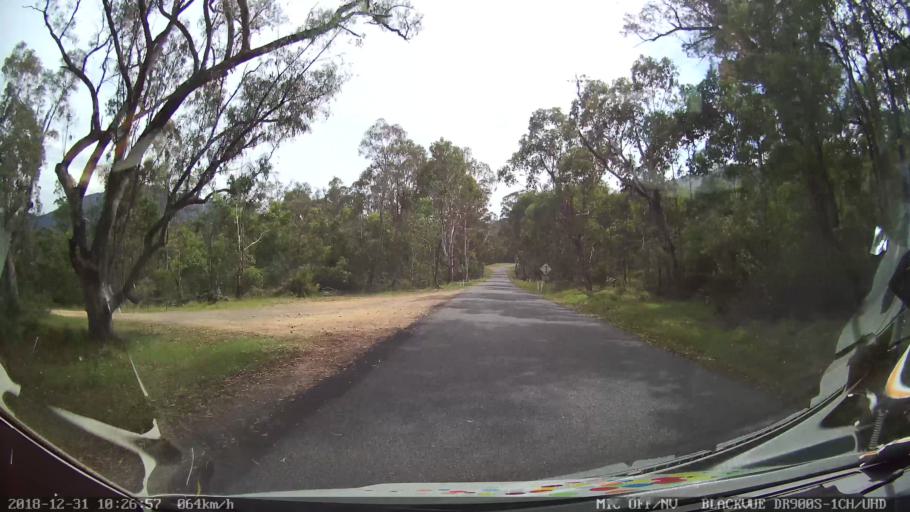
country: AU
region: New South Wales
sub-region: Snowy River
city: Jindabyne
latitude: -36.4902
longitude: 148.1402
